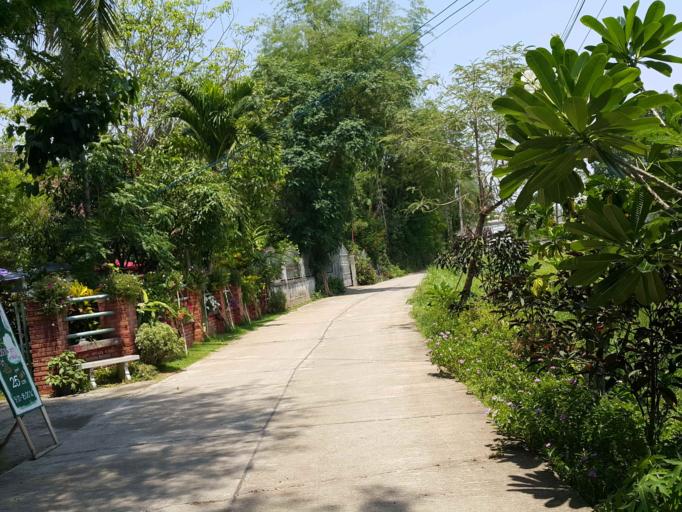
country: TH
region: Chiang Mai
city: San Sai
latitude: 18.8267
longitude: 99.1105
